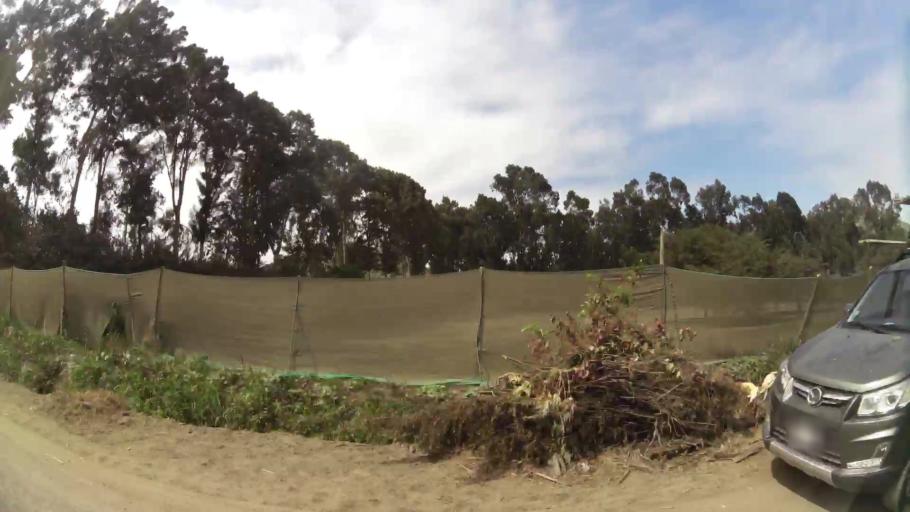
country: PE
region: Lima
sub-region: Provincia de Canete
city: Asia
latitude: -12.7340
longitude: -76.6243
